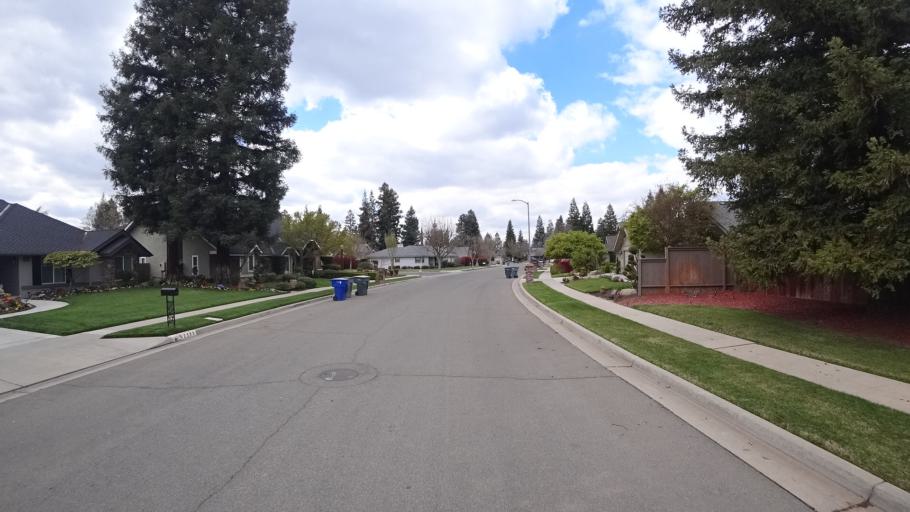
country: US
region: California
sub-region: Fresno County
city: Fresno
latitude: 36.8321
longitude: -119.8112
